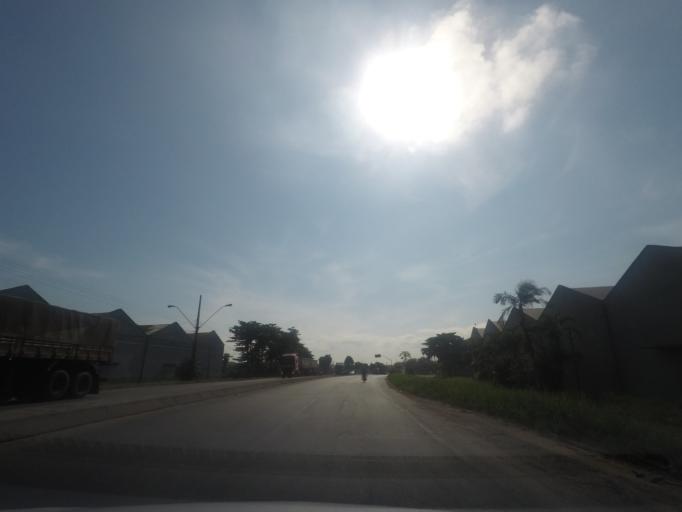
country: BR
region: Parana
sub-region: Paranagua
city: Paranagua
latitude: -25.5167
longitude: -48.5236
